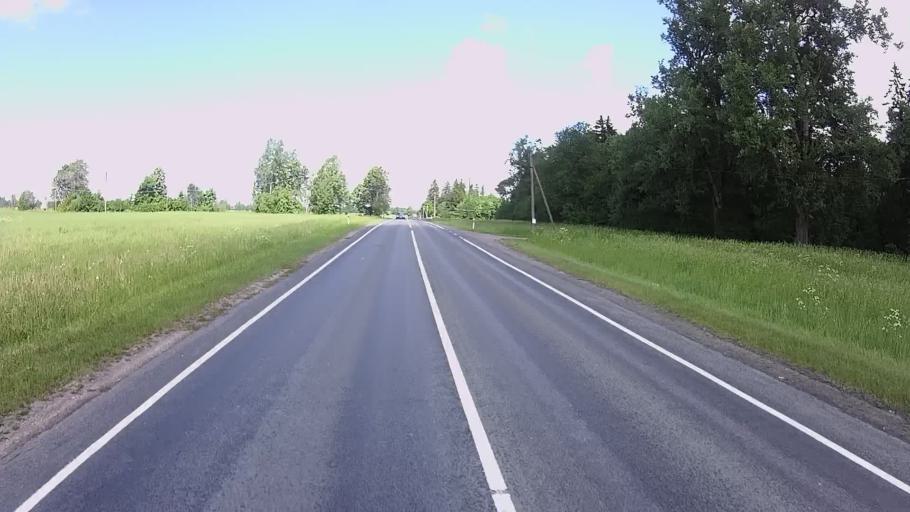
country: EE
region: Viljandimaa
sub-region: Viiratsi vald
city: Viiratsi
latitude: 58.2993
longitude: 25.6807
